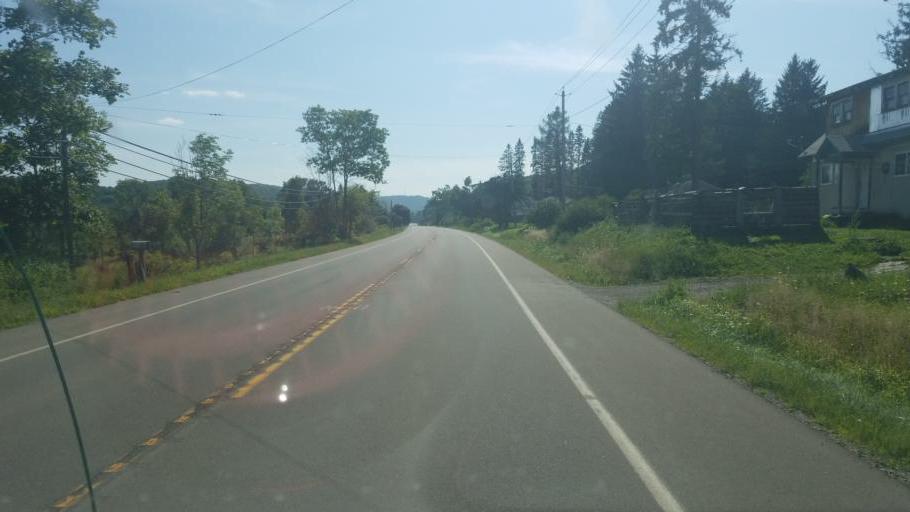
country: US
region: New York
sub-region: Allegany County
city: Wellsville
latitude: 42.0963
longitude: -78.0504
